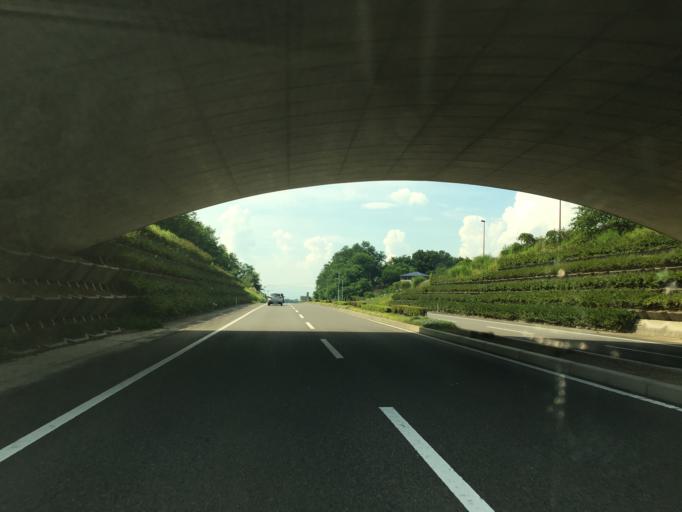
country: JP
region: Fukushima
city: Sukagawa
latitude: 37.2558
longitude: 140.4261
